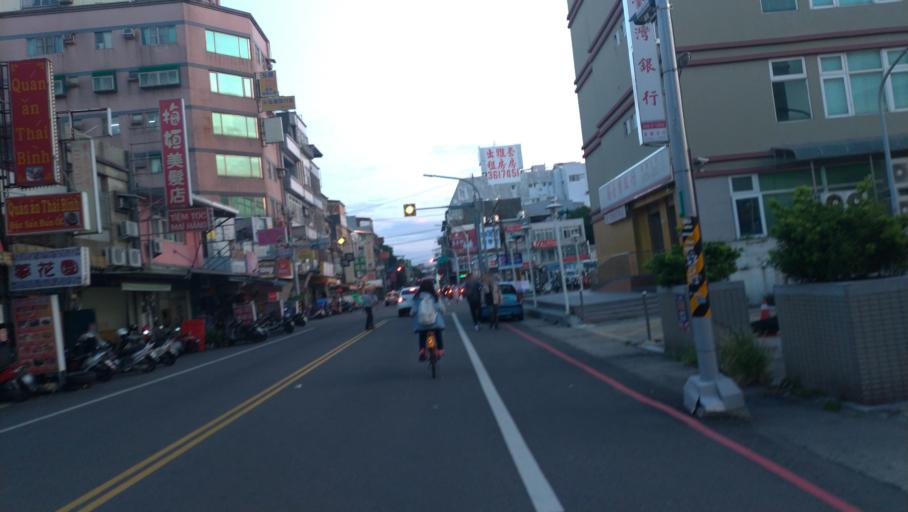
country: TW
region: Taiwan
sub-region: Taoyuan
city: Taoyuan
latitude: 24.9866
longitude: 121.3142
